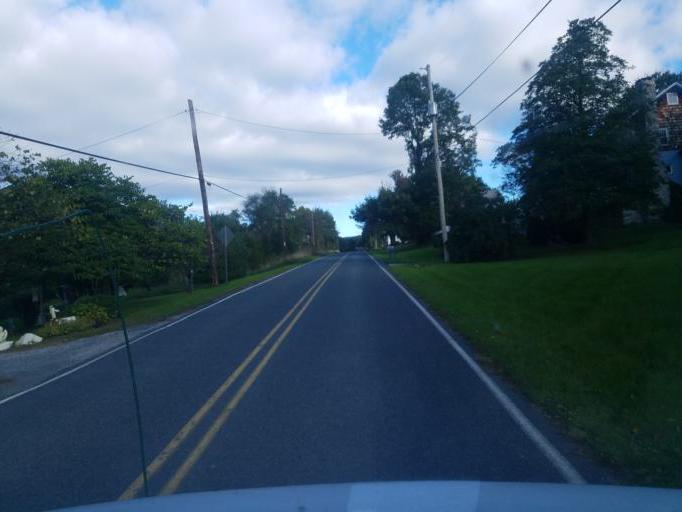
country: US
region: Pennsylvania
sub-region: Adams County
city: Biglerville
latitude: 39.8872
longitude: -77.3685
